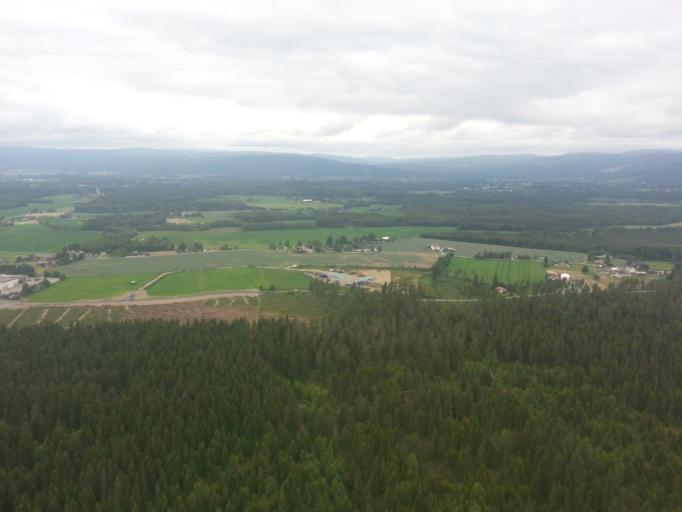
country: NO
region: Akershus
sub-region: Nannestad
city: Maura
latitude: 60.2283
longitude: 11.0986
